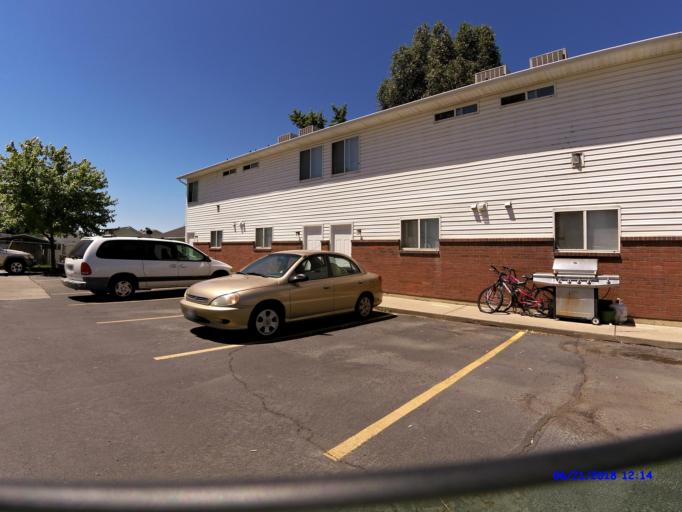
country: US
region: Utah
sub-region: Weber County
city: Harrisville
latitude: 41.2852
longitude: -112.0011
